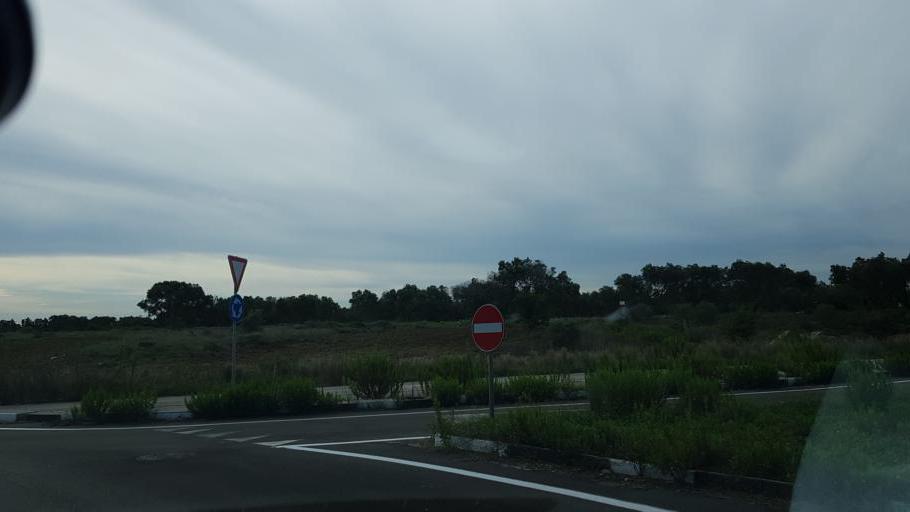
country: IT
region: Apulia
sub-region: Provincia di Lecce
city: Vernole
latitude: 40.3289
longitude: 18.3368
